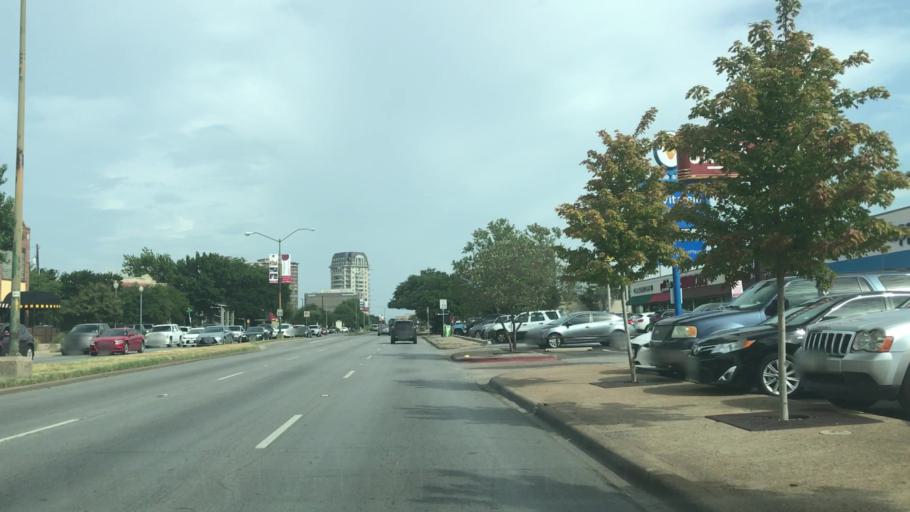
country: US
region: Texas
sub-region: Dallas County
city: Highland Park
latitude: 32.8156
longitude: -96.8100
